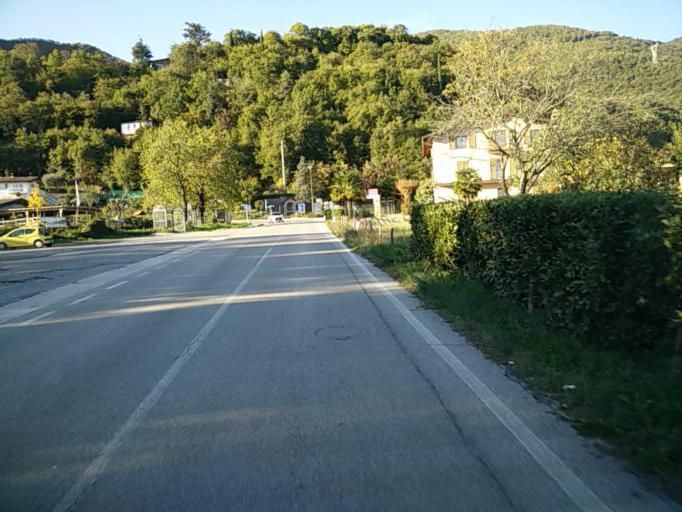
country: IT
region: Lombardy
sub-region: Provincia di Brescia
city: Gargnano
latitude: 45.6864
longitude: 10.6409
